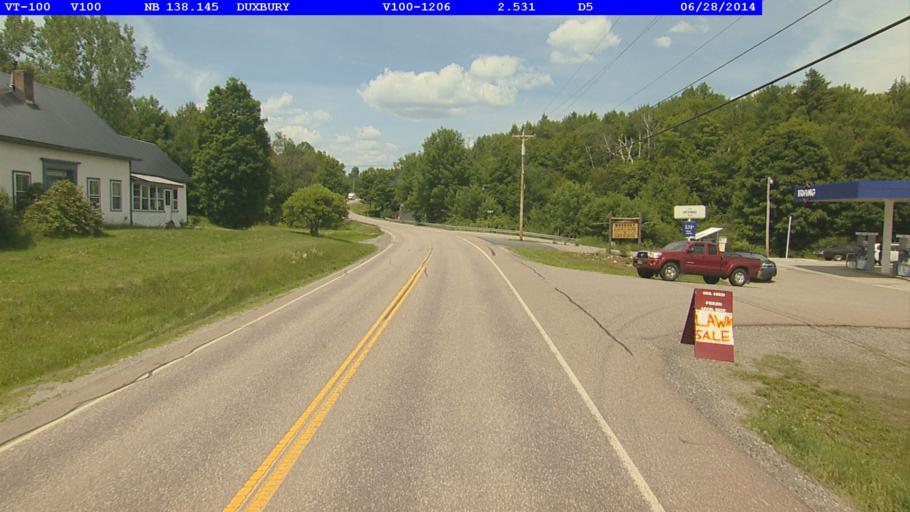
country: US
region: Vermont
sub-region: Washington County
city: Waterbury
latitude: 44.2820
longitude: -72.7825
